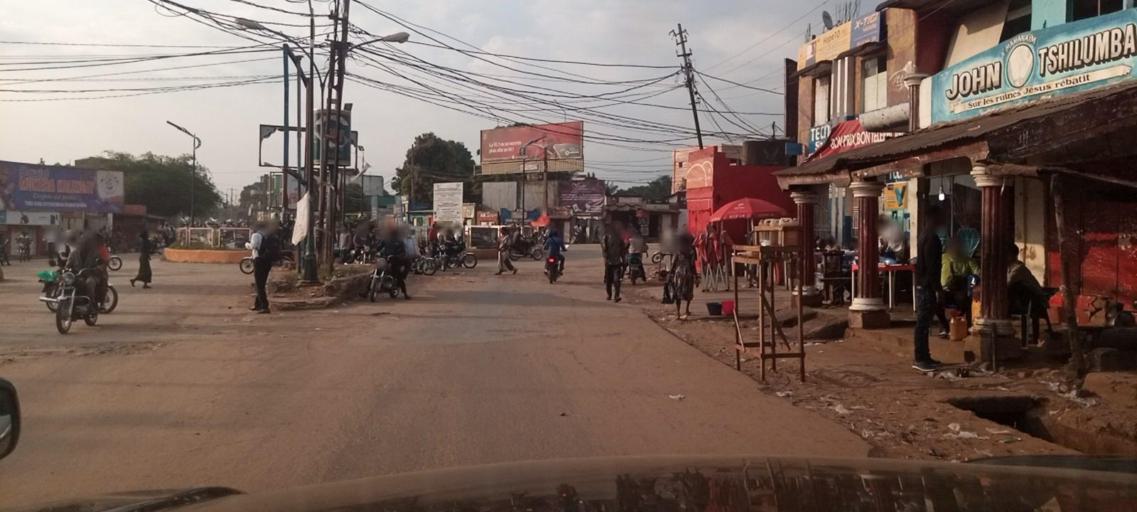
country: CD
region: Kasai-Oriental
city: Mbuji-Mayi
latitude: -6.1343
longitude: 23.6100
